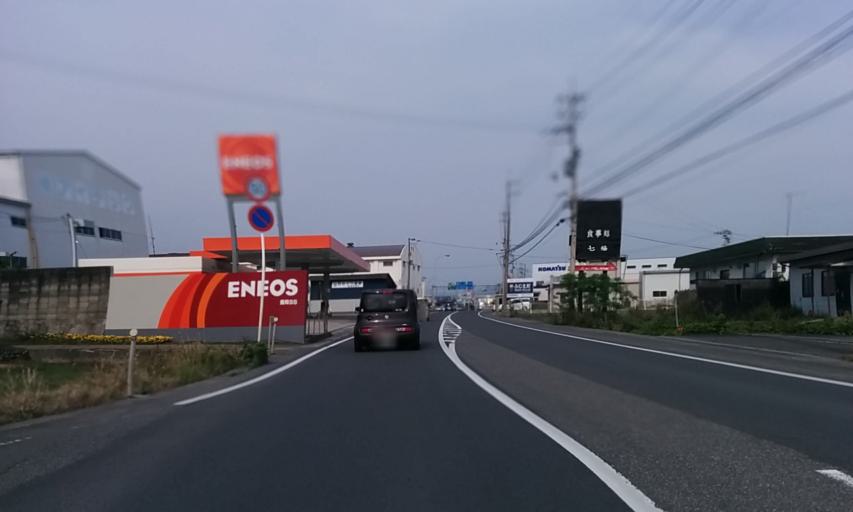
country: JP
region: Ehime
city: Kawanoecho
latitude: 33.9652
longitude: 133.4710
